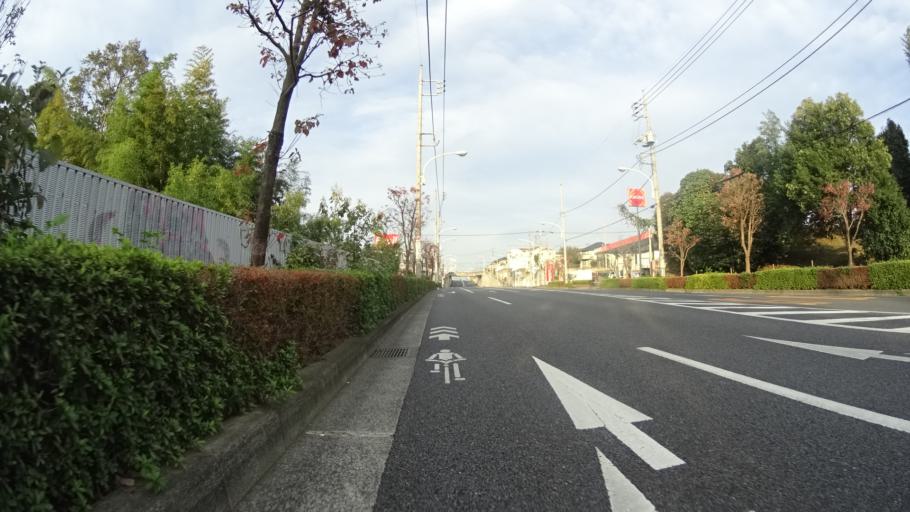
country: JP
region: Tokyo
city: Fussa
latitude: 35.7236
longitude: 139.2880
